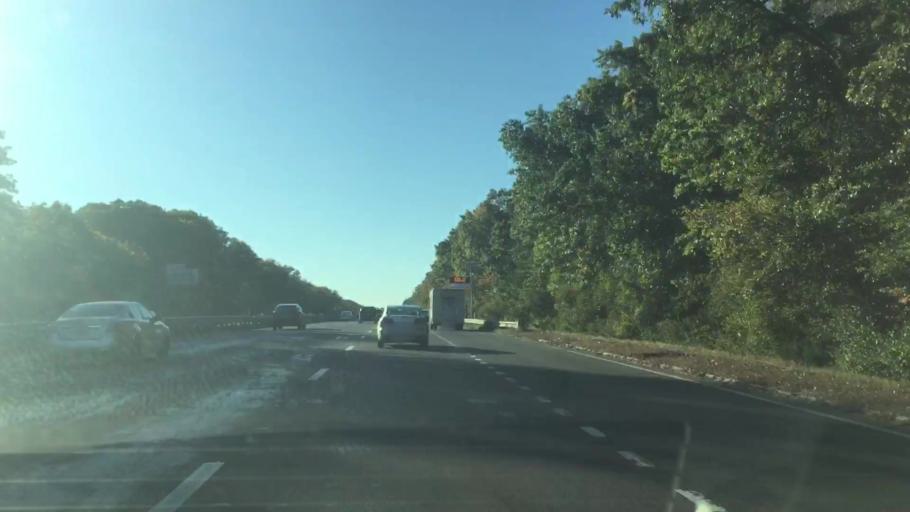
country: US
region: Massachusetts
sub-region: Essex County
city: Methuen
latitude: 42.6868
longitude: -71.2049
